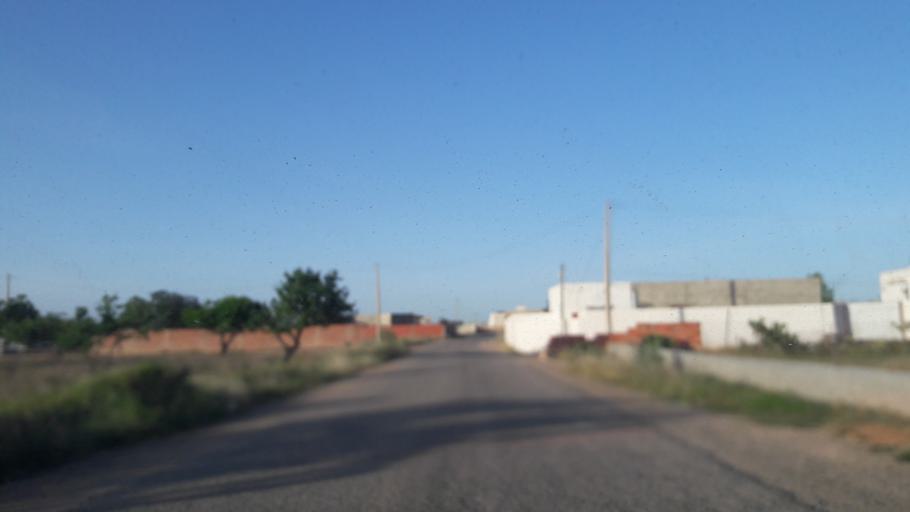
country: TN
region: Safaqis
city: Sfax
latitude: 34.8191
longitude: 10.7376
